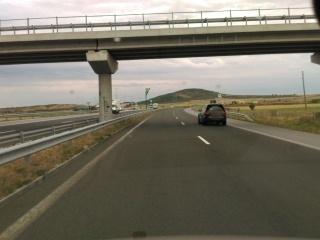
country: BG
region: Yambol
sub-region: Obshtina Yambol
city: Yambol
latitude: 42.5444
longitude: 26.4441
